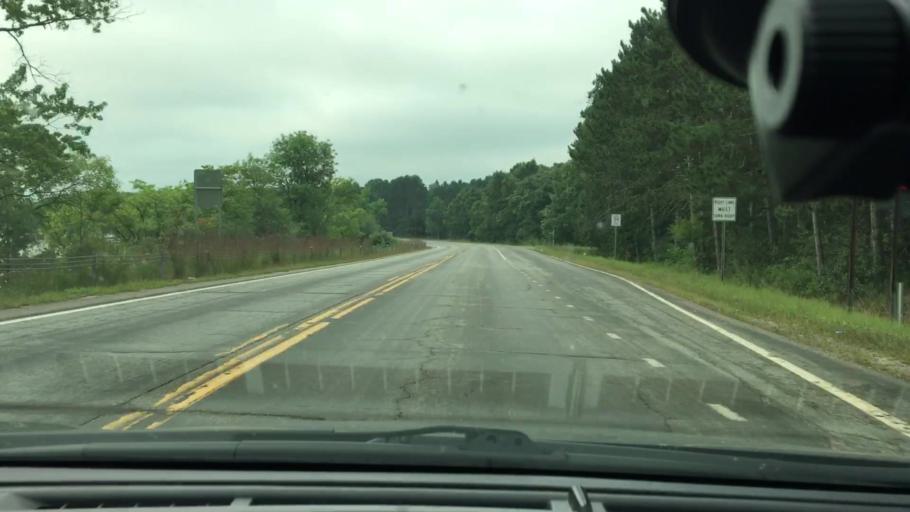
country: US
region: Minnesota
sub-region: Crow Wing County
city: Cross Lake
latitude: 46.7261
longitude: -93.9583
